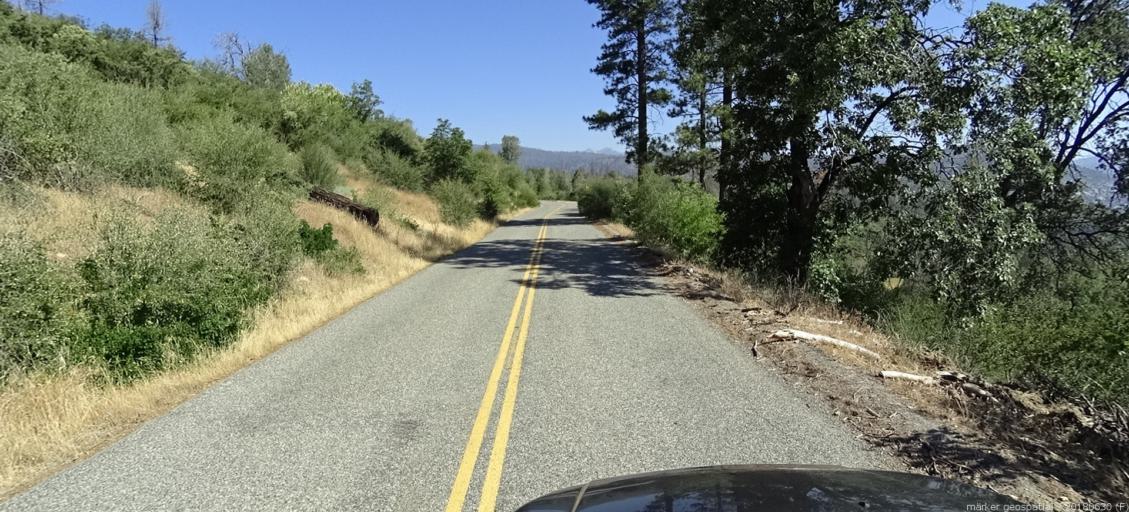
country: US
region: California
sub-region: Fresno County
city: Auberry
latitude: 37.2185
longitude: -119.3513
